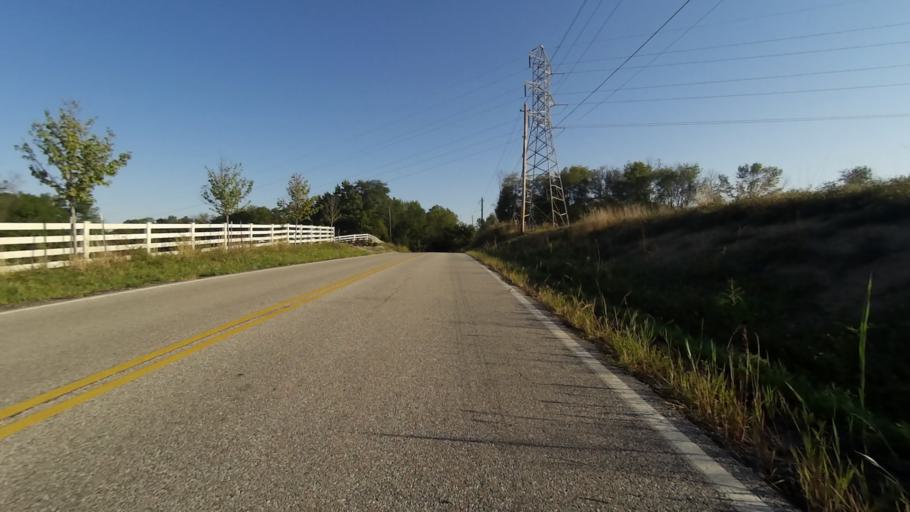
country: US
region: Ohio
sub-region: Portage County
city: Kent
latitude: 41.1966
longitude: -81.3671
